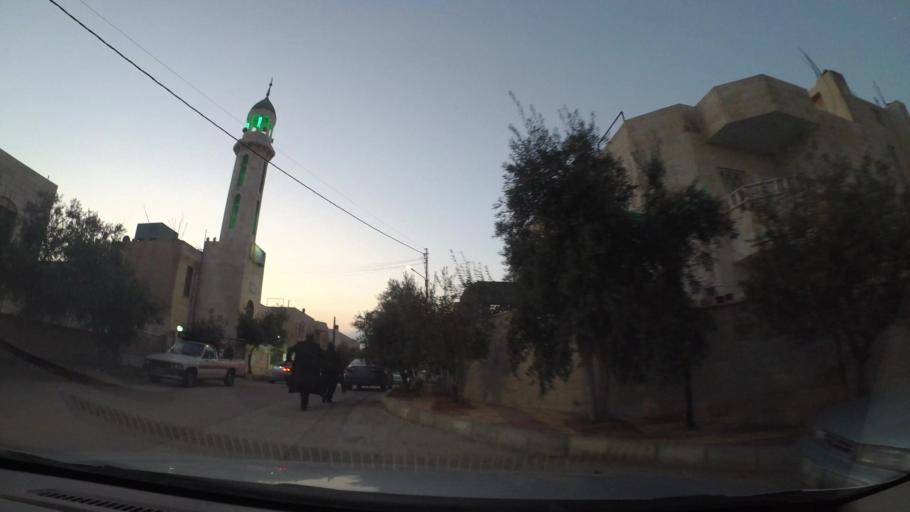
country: JO
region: Amman
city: Al Bunayyat ash Shamaliyah
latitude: 31.8871
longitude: 35.9221
